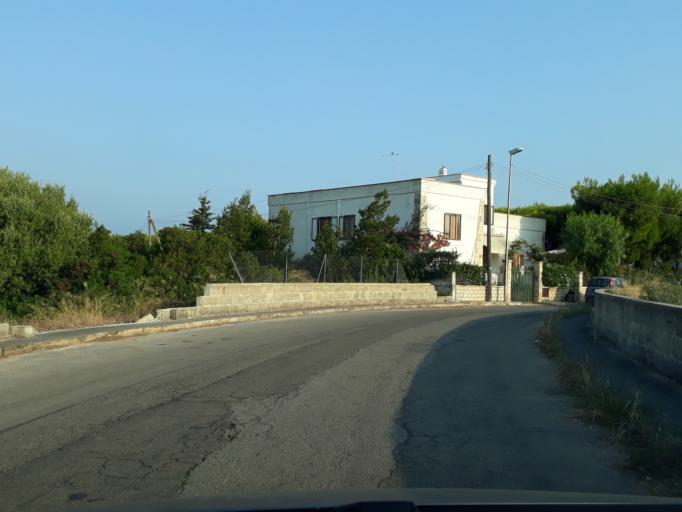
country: IT
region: Apulia
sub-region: Provincia di Brindisi
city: Carovigno
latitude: 40.7546
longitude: 17.7044
